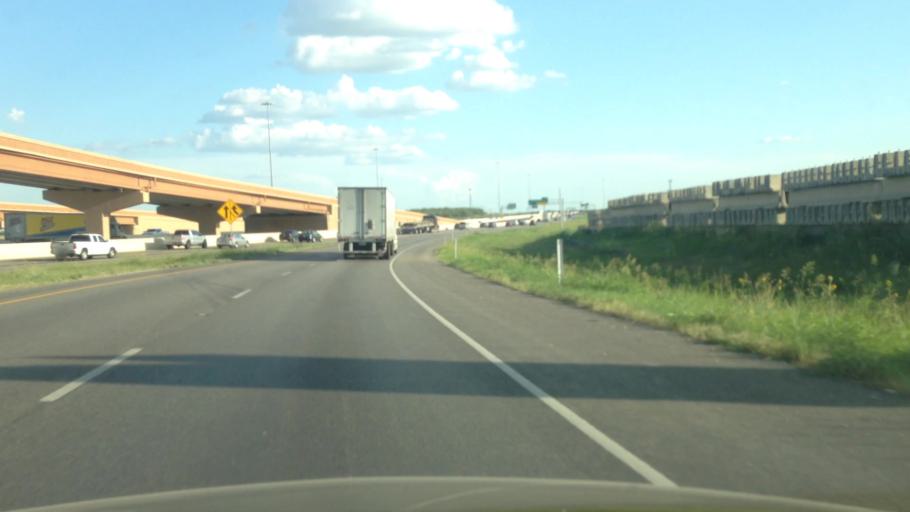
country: US
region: Texas
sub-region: Tarrant County
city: Blue Mound
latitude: 32.8858
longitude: -97.3186
